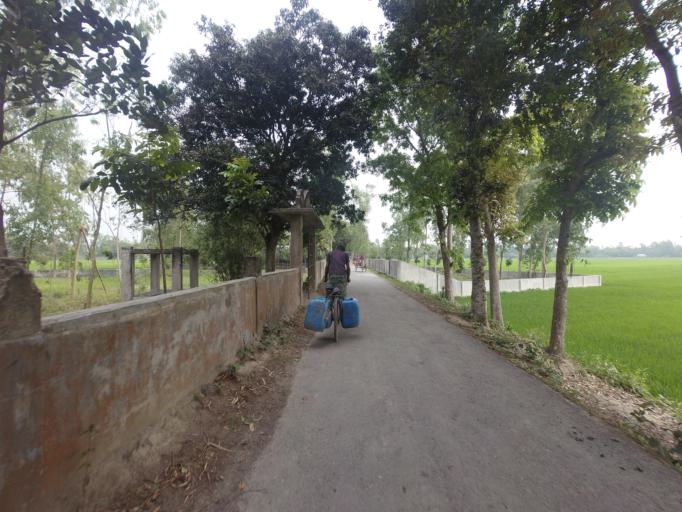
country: BD
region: Rajshahi
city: Sirajganj
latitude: 24.3258
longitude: 89.6764
